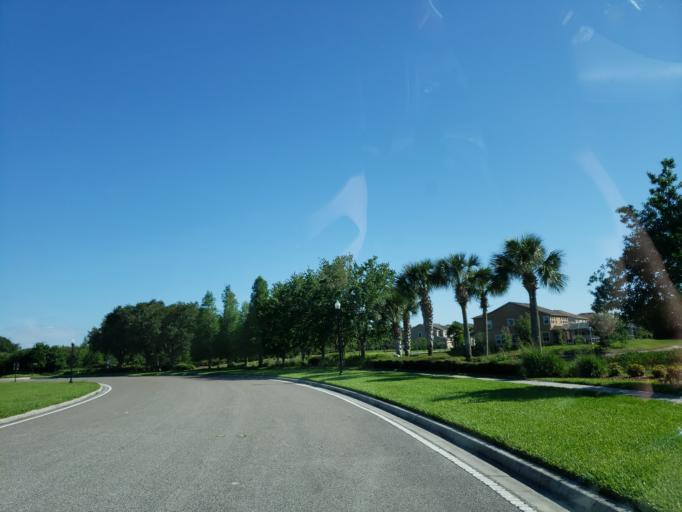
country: US
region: Florida
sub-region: Pasco County
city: Wesley Chapel
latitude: 28.2241
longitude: -82.3608
